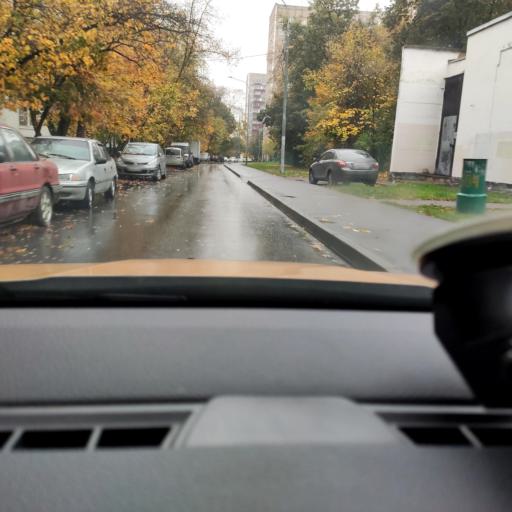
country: RU
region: Moscow
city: Zapadnoye Degunino
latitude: 55.8388
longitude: 37.5352
